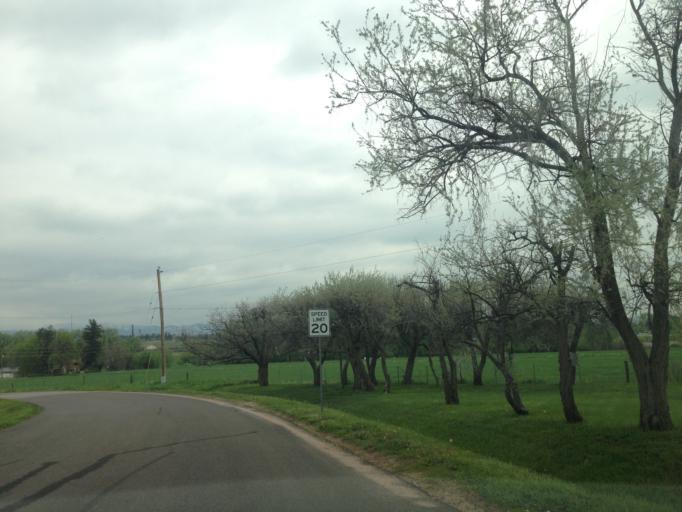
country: US
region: Colorado
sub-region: Boulder County
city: Louisville
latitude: 40.0071
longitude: -105.1755
